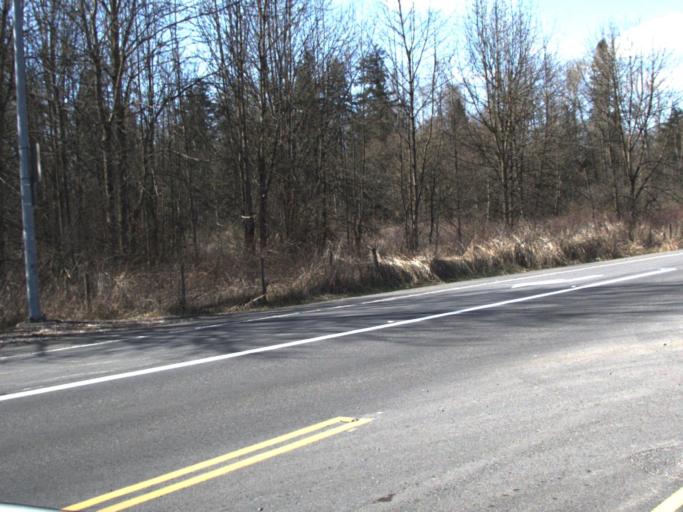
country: US
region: Washington
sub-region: King County
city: Lake Morton-Berrydale
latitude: 47.2402
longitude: -122.1102
